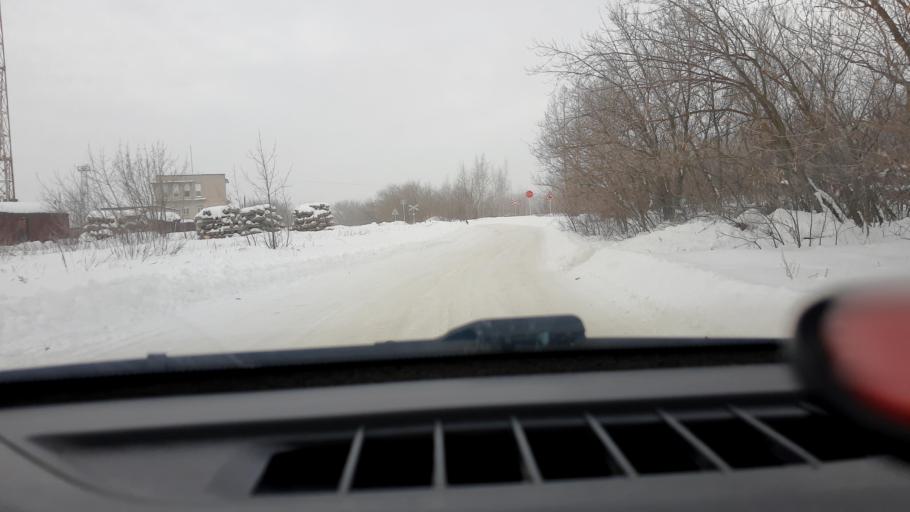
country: RU
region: Nizjnij Novgorod
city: Babino
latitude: 56.2623
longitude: 43.6092
